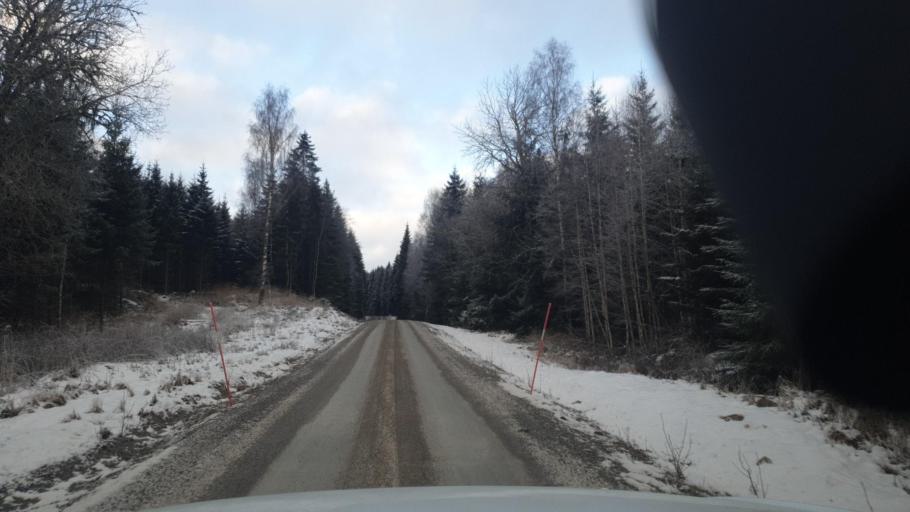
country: SE
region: Vaermland
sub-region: Eda Kommun
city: Charlottenberg
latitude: 60.0263
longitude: 12.6333
